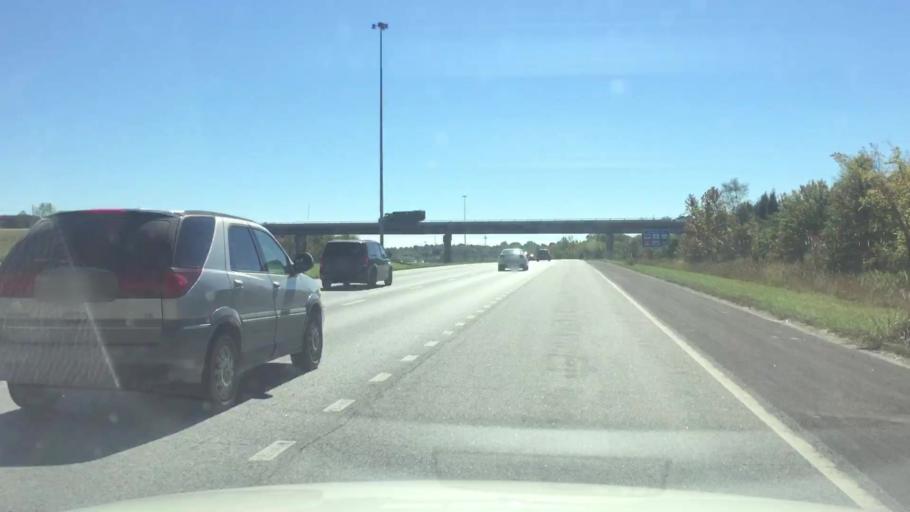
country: US
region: Kansas
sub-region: Wyandotte County
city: Edwardsville
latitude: 39.0104
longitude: -94.7854
